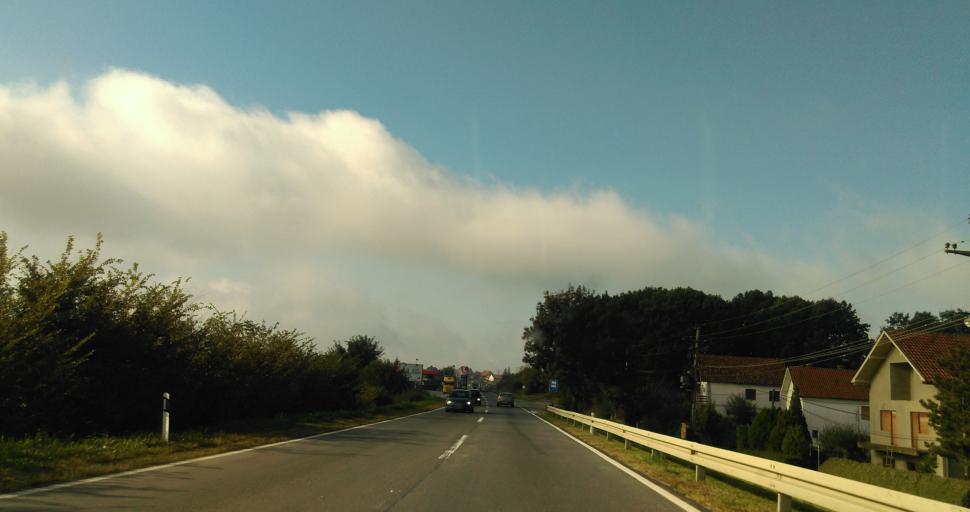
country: RS
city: Vranic
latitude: 44.5726
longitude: 20.3068
